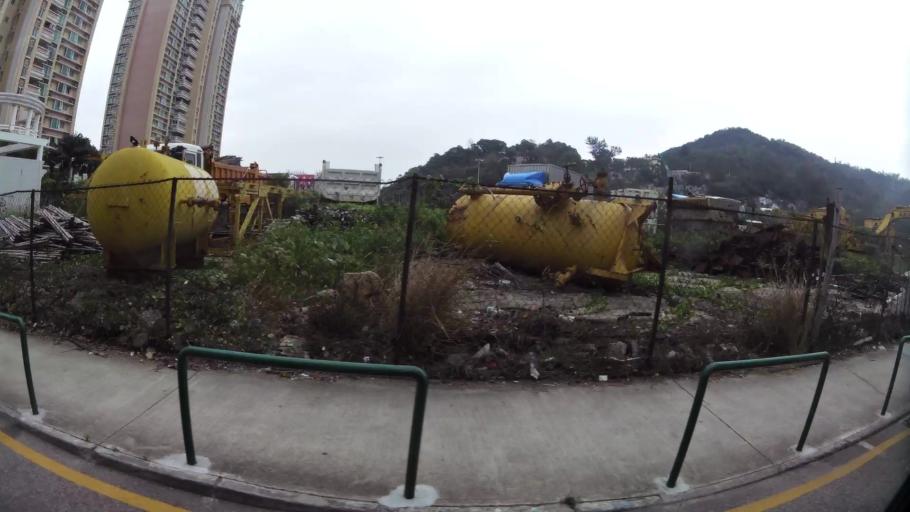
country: MO
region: Macau
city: Macau
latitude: 22.1643
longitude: 113.5611
